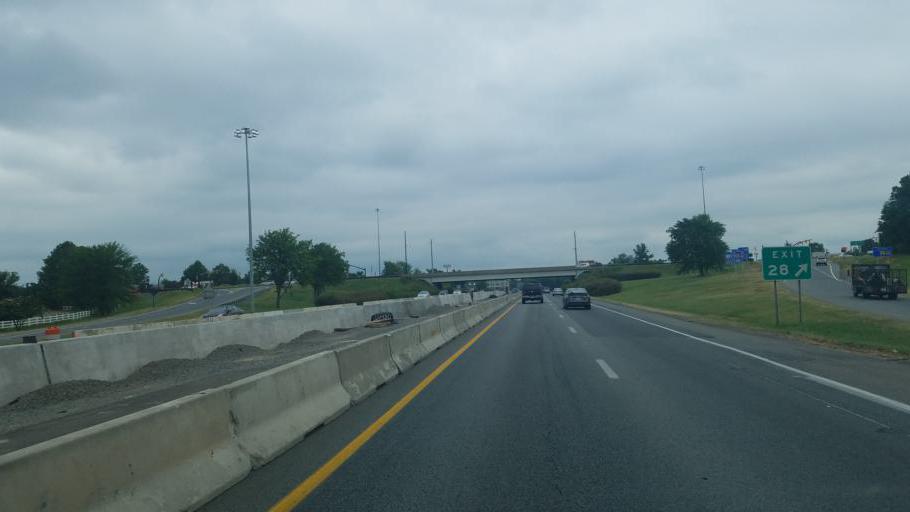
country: US
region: North Carolina
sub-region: Mecklenburg County
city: Cornelius
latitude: 35.4809
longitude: -80.8747
